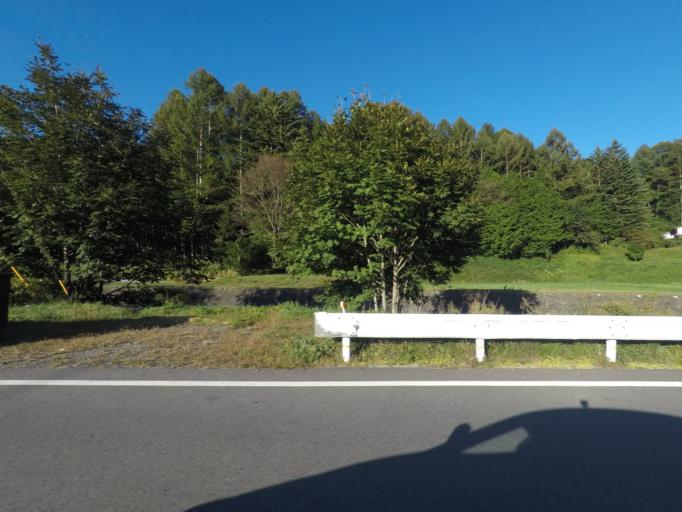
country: JP
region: Nagano
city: Tatsuno
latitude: 35.9702
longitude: 137.7591
